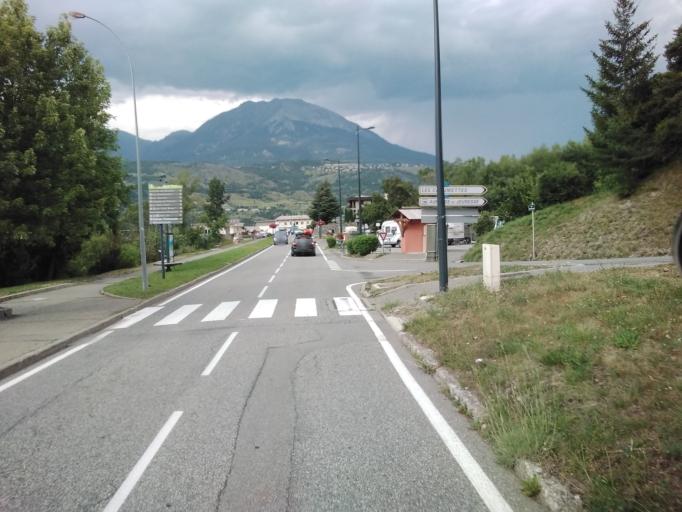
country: FR
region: Provence-Alpes-Cote d'Azur
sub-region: Departement des Hautes-Alpes
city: Embrun
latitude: 44.5246
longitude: 6.4004
